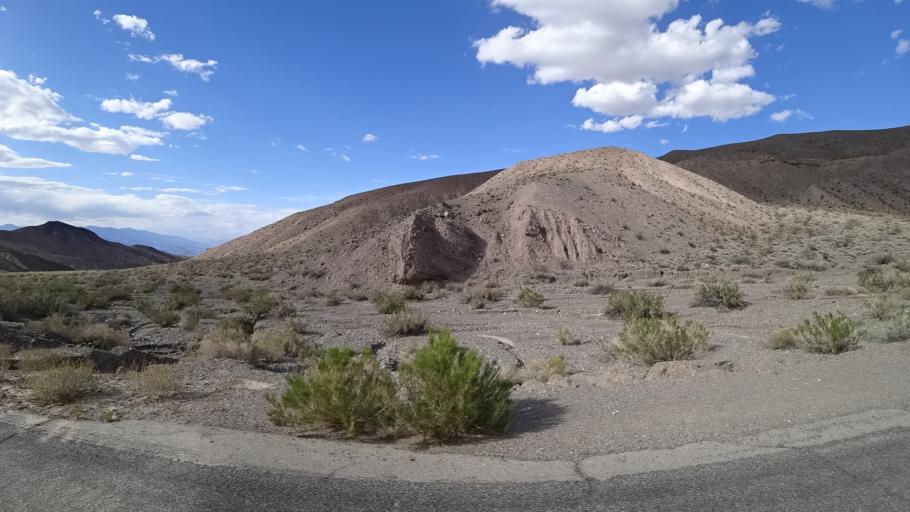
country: US
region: Nevada
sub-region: Nye County
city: Beatty
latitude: 36.4514
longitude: -117.2036
